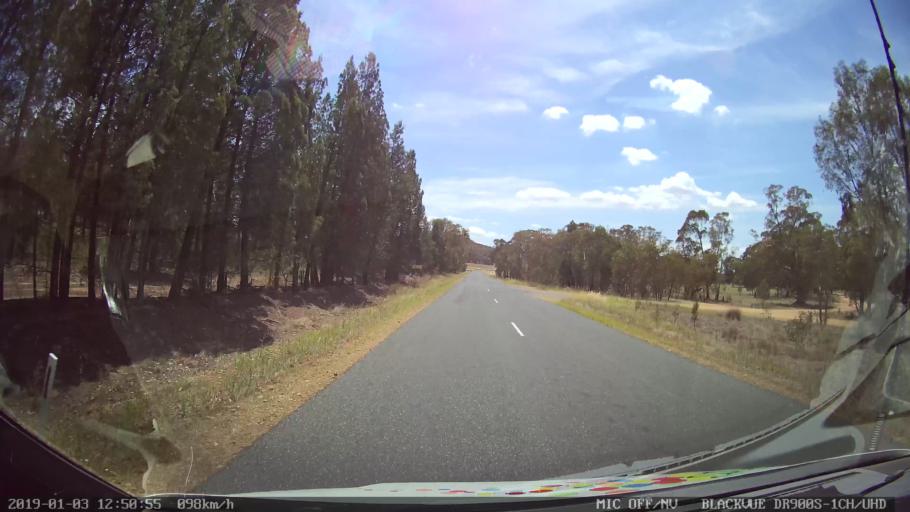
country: AU
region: New South Wales
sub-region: Weddin
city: Grenfell
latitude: -33.6857
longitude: 148.2749
